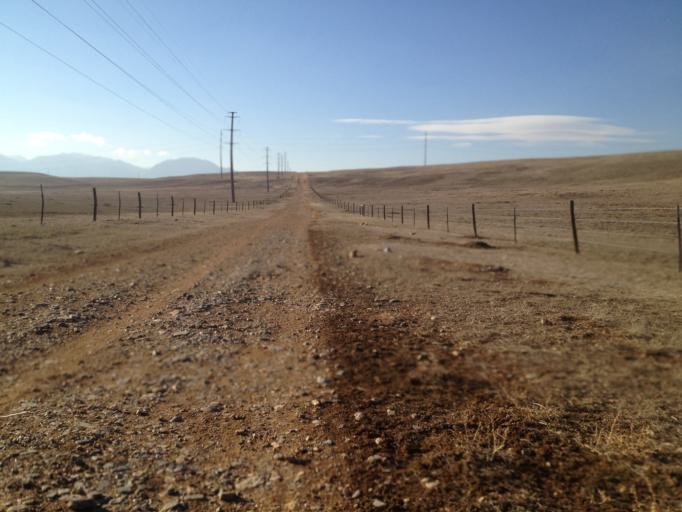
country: US
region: Colorado
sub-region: Boulder County
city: Superior
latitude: 39.9287
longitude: -105.1770
